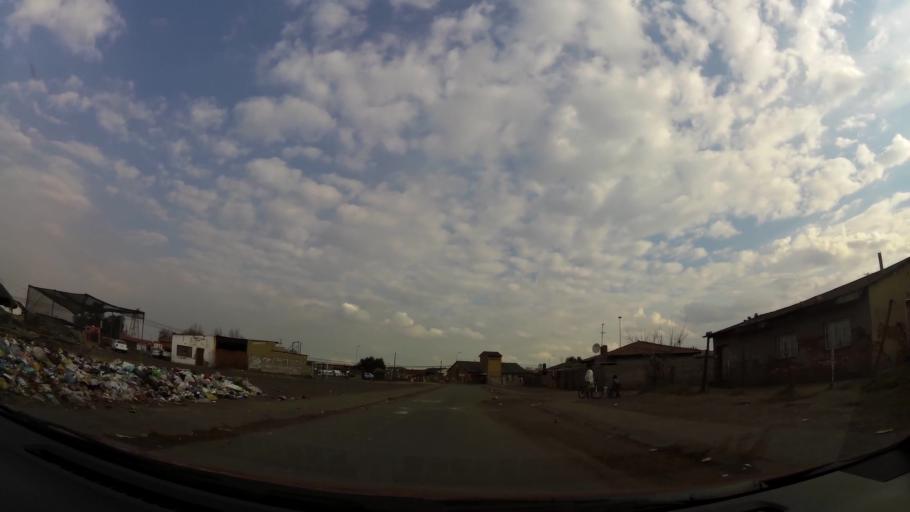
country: ZA
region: Gauteng
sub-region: Sedibeng District Municipality
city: Vanderbijlpark
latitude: -26.6958
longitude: 27.8734
